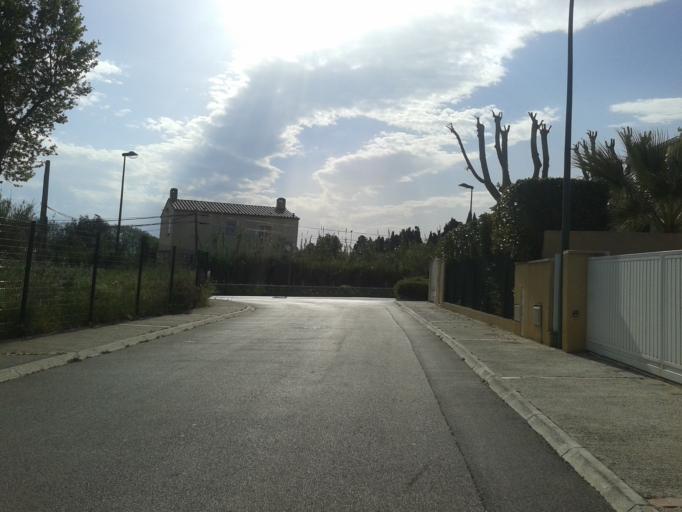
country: FR
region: Languedoc-Roussillon
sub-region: Departement des Pyrenees-Orientales
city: Pezilla-la-Riviere
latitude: 42.6984
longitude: 2.7651
